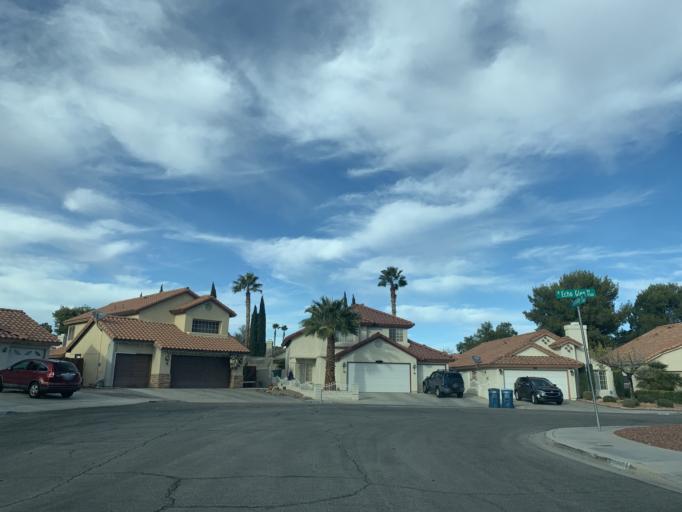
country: US
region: Nevada
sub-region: Clark County
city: Summerlin South
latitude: 36.1313
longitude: -115.3040
